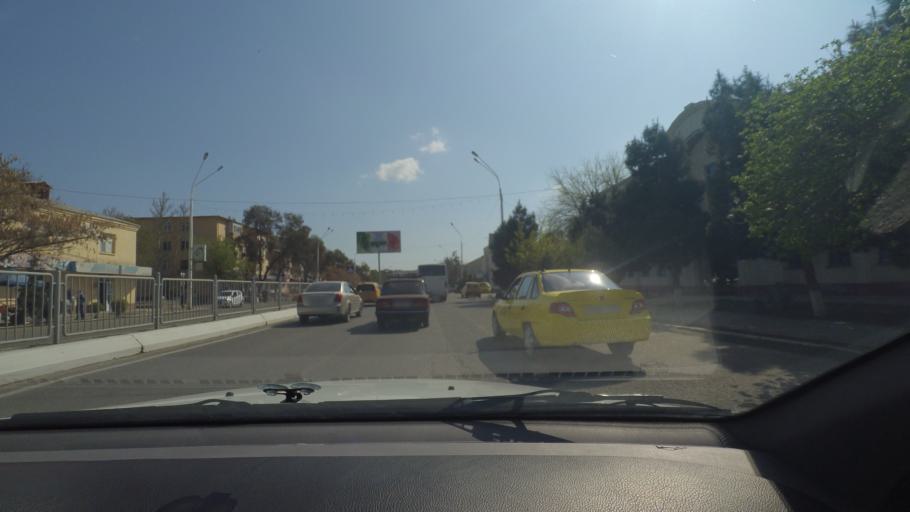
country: UZ
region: Bukhara
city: Bukhara
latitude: 39.7650
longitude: 64.4305
